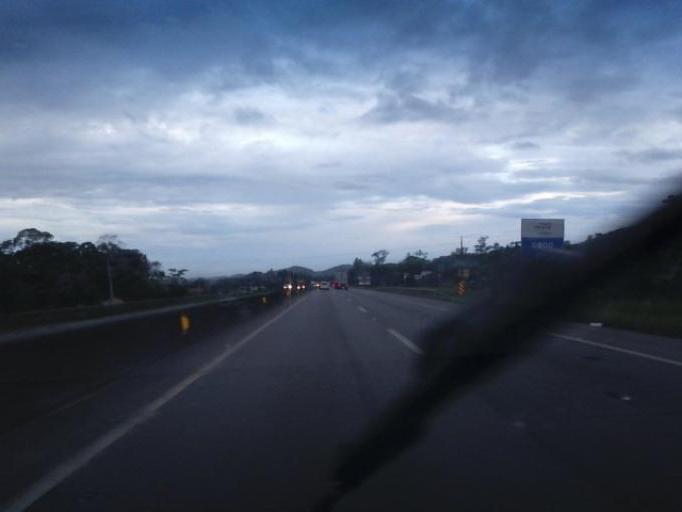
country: BR
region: Santa Catarina
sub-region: Joinville
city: Joinville
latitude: -26.0331
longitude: -48.8606
